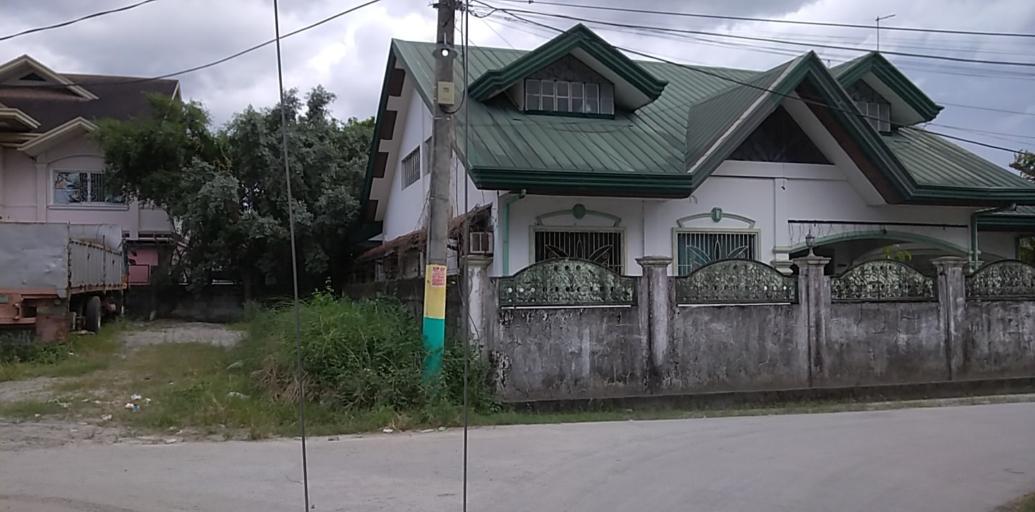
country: PH
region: Central Luzon
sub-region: Province of Pampanga
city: Porac
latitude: 15.0624
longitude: 120.5422
